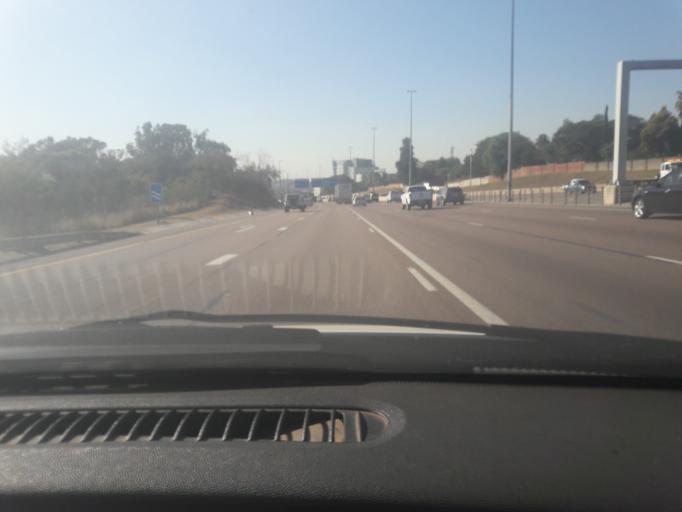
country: ZA
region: Gauteng
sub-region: City of Tshwane Metropolitan Municipality
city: Pretoria
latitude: -25.7920
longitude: 28.2677
